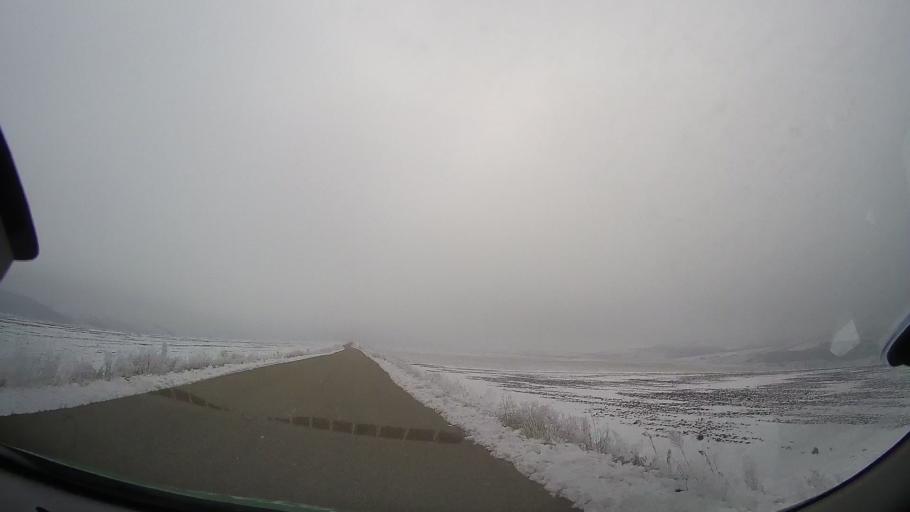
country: RO
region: Vaslui
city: Coroiesti
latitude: 46.2279
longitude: 27.4782
